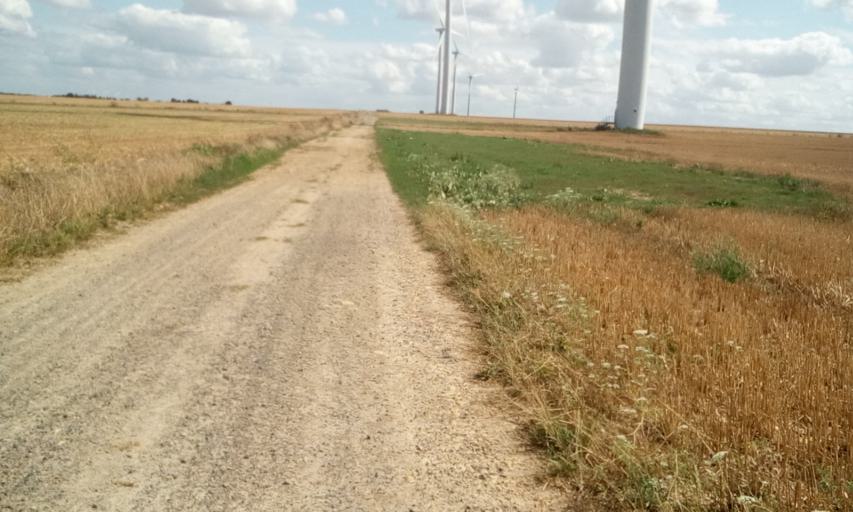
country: FR
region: Lower Normandy
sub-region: Departement du Calvados
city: Bellengreville
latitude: 49.1050
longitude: -0.2373
